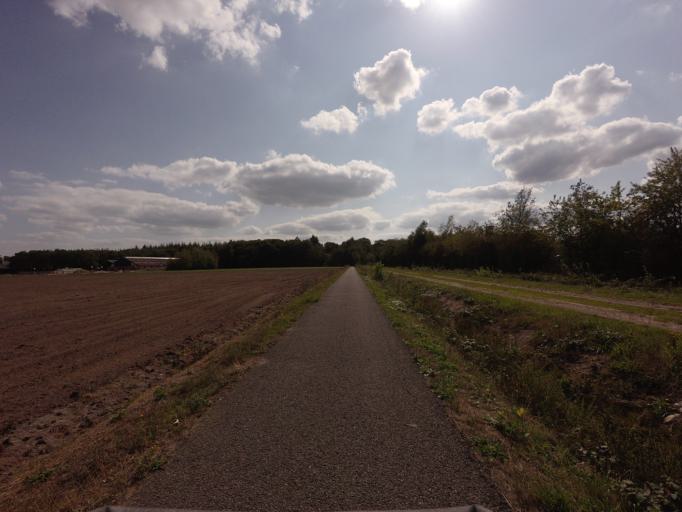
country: NL
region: Drenthe
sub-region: Gemeente Westerveld
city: Dwingeloo
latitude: 52.8407
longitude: 6.4679
